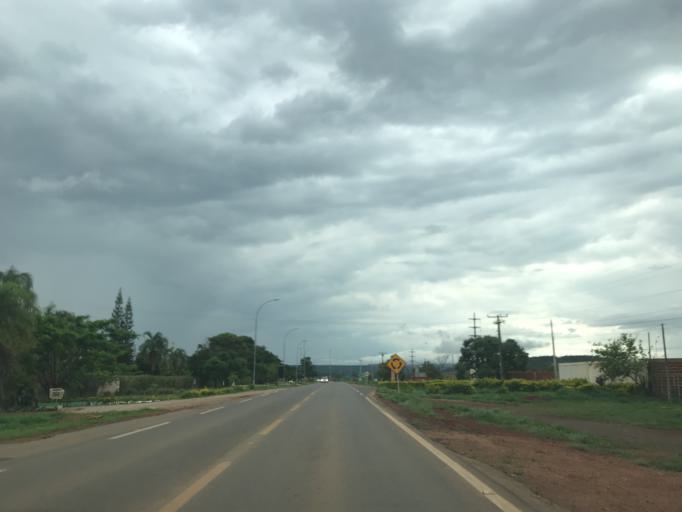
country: BR
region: Goias
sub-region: Planaltina
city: Planaltina
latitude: -15.6404
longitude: -47.6881
